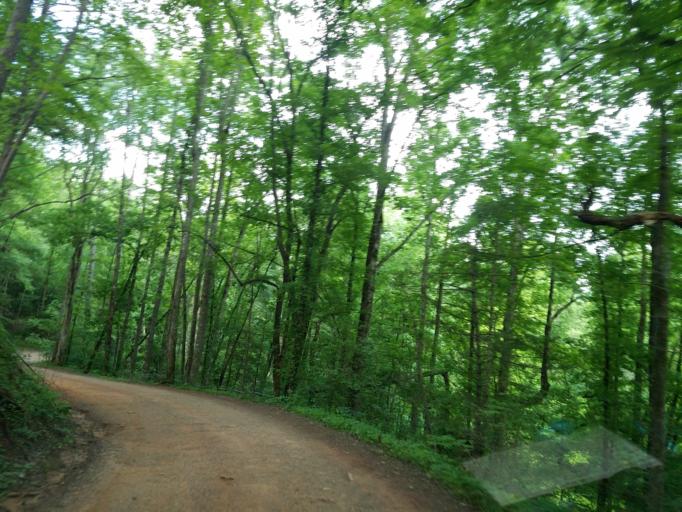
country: US
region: Georgia
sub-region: Lumpkin County
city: Dahlonega
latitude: 34.5774
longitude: -84.1275
